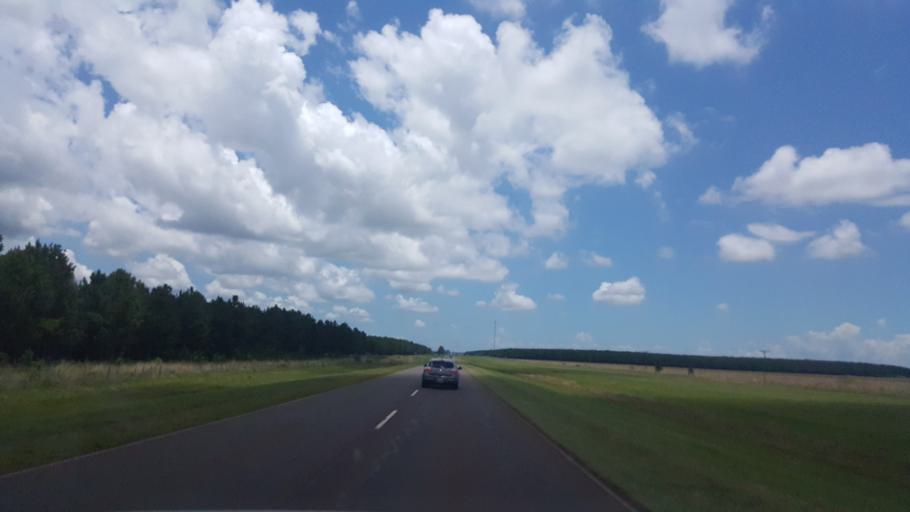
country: PY
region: Itapua
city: San Juan del Parana
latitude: -27.5135
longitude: -56.1422
